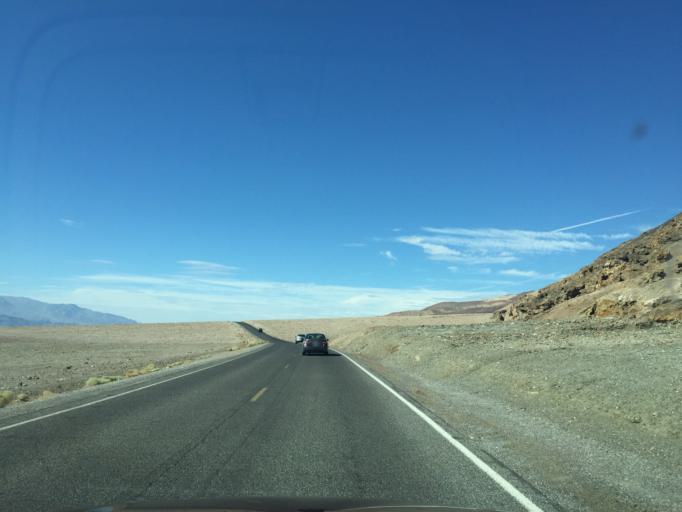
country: US
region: Nevada
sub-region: Nye County
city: Beatty
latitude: 36.2536
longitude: -116.7744
